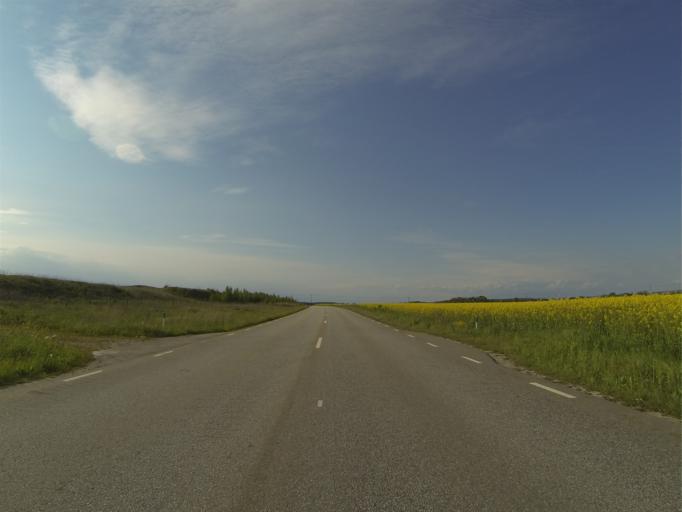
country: SE
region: Skane
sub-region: Lunds Kommun
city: Lund
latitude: 55.7034
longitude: 13.3037
